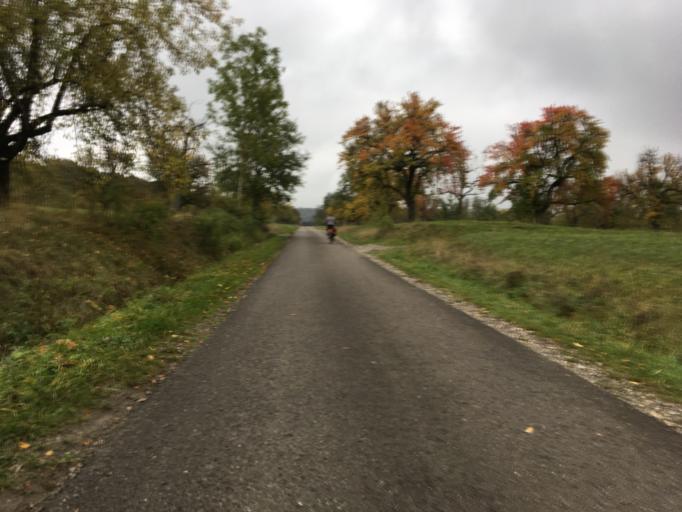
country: DE
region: Baden-Wuerttemberg
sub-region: Tuebingen Region
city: Nehren
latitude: 48.4272
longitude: 9.0771
